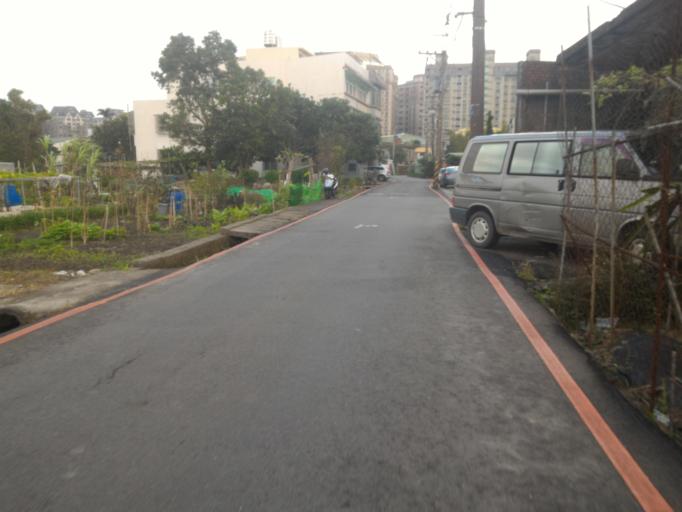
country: TW
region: Taiwan
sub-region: Taoyuan
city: Taoyuan
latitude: 24.9424
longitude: 121.3816
